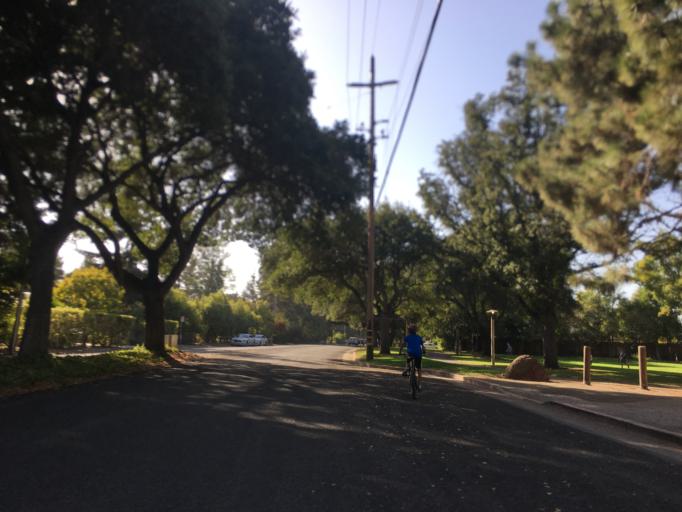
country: US
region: California
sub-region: Santa Clara County
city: Loyola
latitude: 37.3524
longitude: -122.0791
